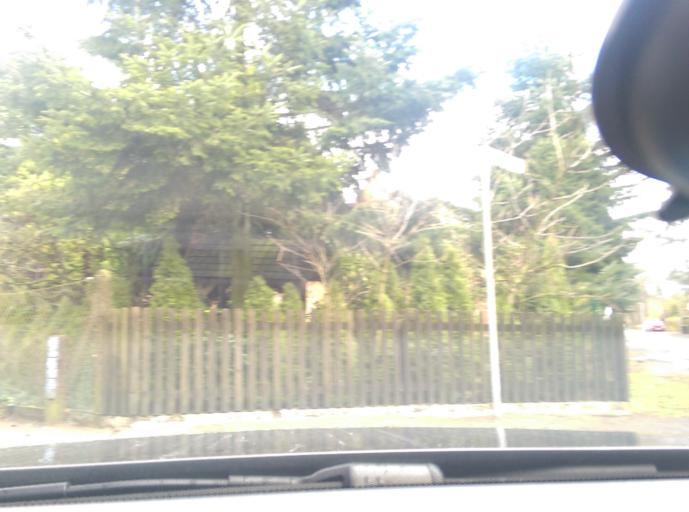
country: DE
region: Lower Saxony
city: Lindwedel
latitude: 52.5716
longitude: 9.5996
